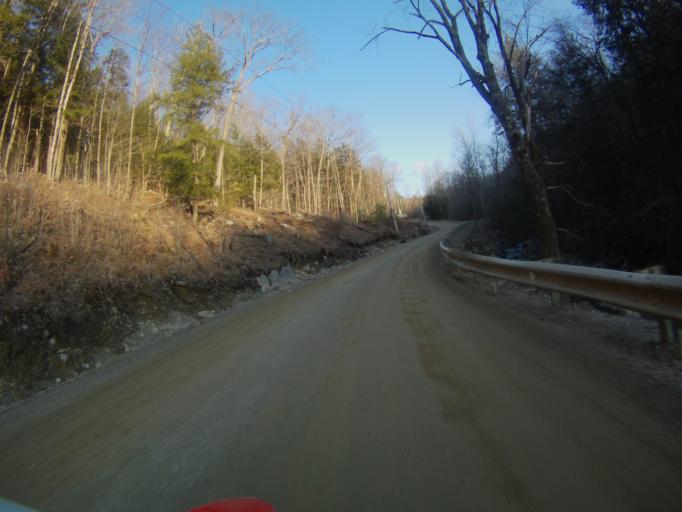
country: US
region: Vermont
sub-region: Addison County
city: Bristol
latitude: 44.0773
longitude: -73.0628
